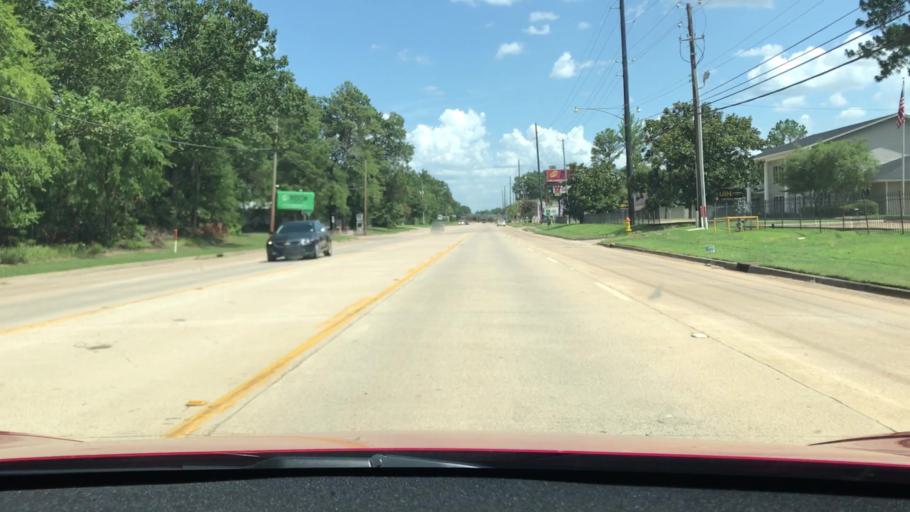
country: US
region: Louisiana
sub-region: Bossier Parish
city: Bossier City
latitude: 32.4259
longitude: -93.7406
